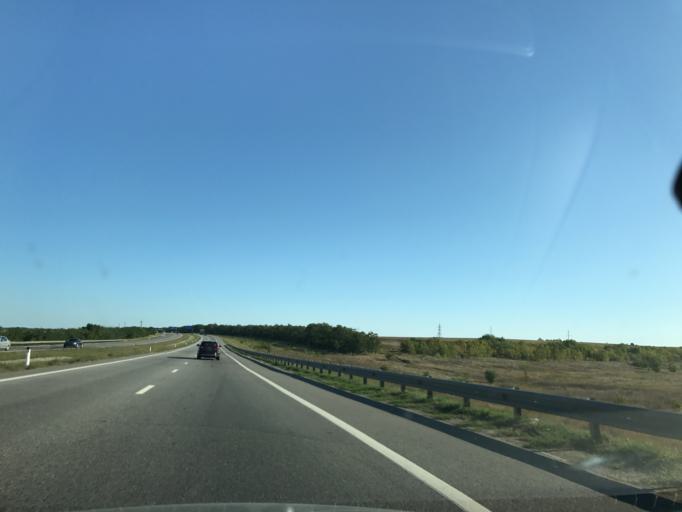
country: RU
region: Rostov
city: Tarasovskiy
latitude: 48.7800
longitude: 40.3894
